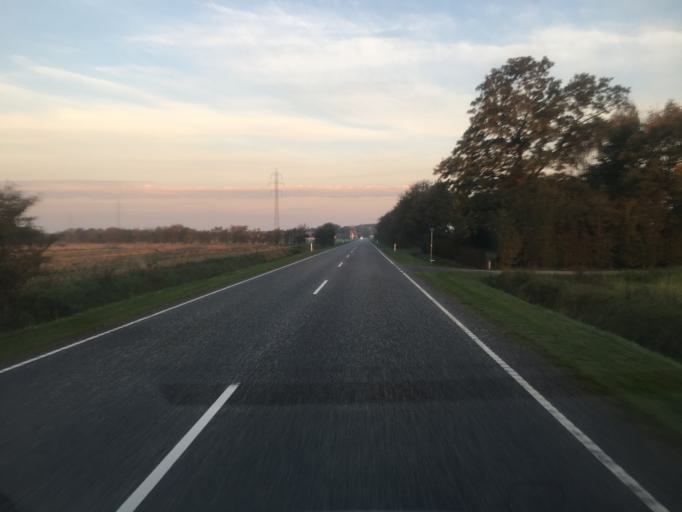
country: DK
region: South Denmark
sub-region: Tonder Kommune
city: Logumkloster
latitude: 55.0368
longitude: 9.0346
